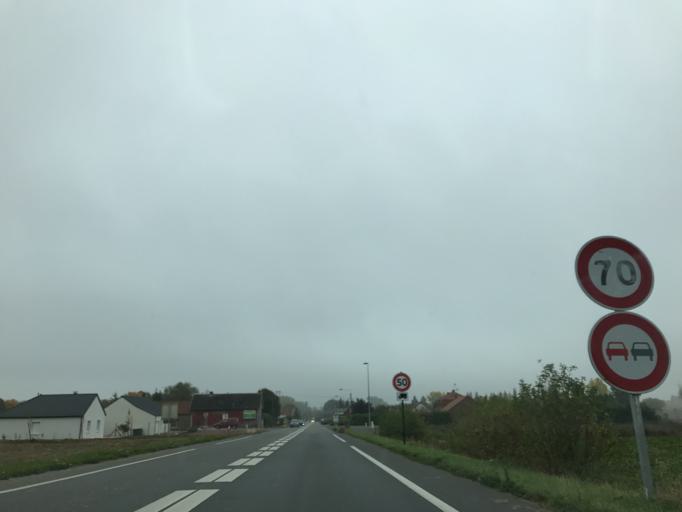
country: FR
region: Nord-Pas-de-Calais
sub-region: Departement du Pas-de-Calais
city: Beaurains
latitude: 50.2210
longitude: 2.8099
